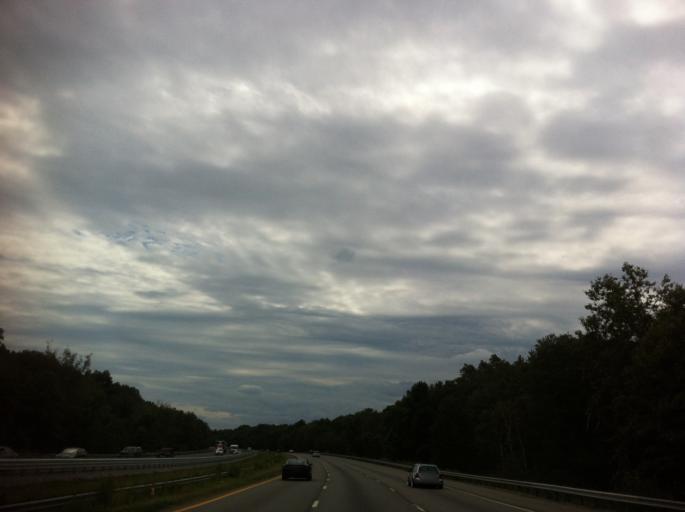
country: US
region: New Jersey
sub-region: Essex County
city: Fairfield
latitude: 40.8937
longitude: -74.2768
